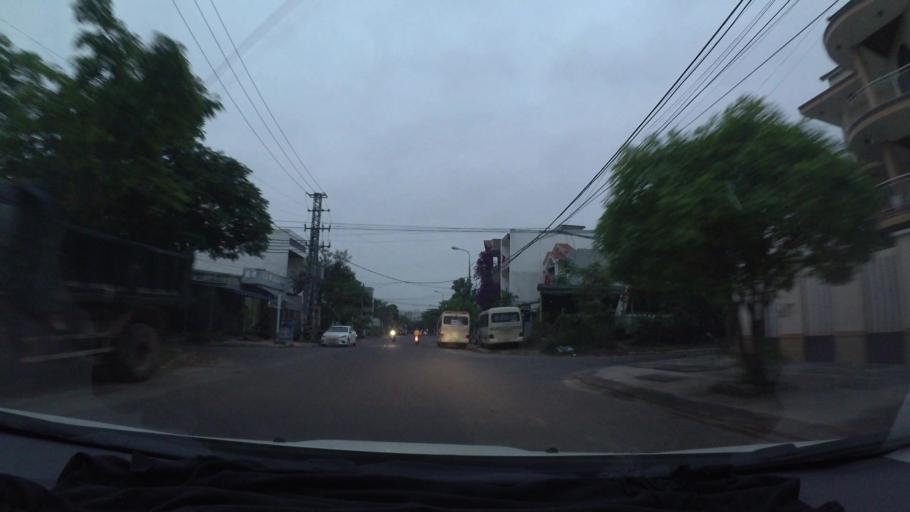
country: VN
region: Da Nang
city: Lien Chieu
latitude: 16.0505
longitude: 108.1725
